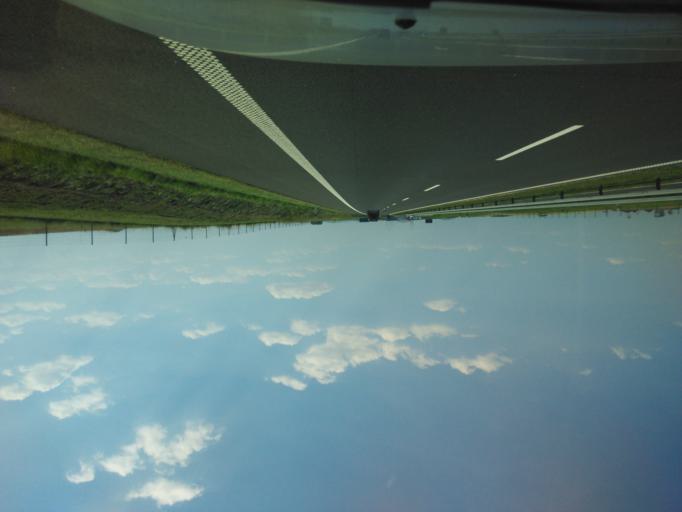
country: PL
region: West Pomeranian Voivodeship
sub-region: Powiat pyrzycki
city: Bielice
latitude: 53.1339
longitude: 14.7252
